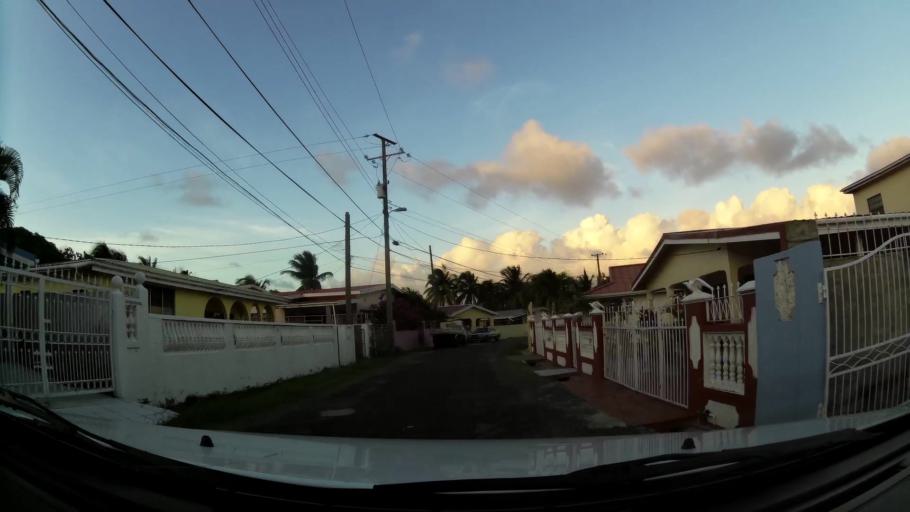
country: LC
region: Gros-Islet
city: Gros Islet
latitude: 14.0667
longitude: -60.9558
